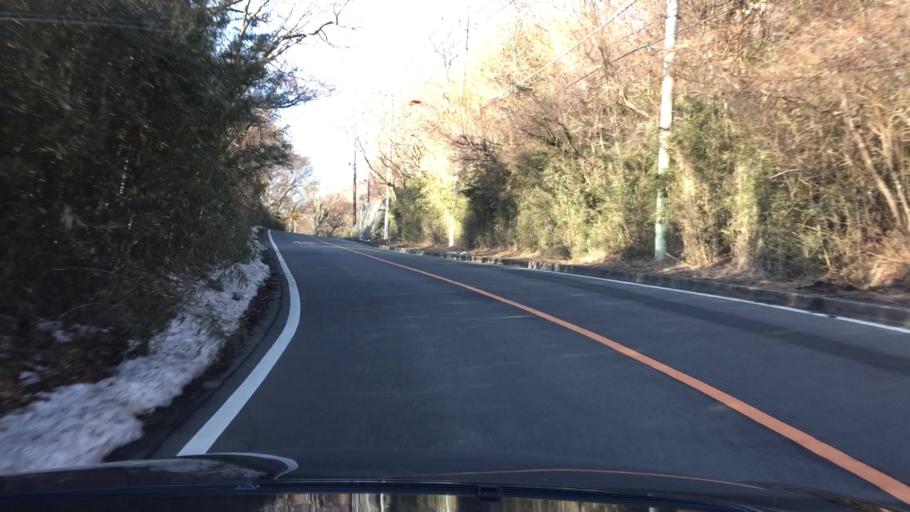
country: JP
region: Kanagawa
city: Hakone
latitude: 35.2197
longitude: 139.0057
